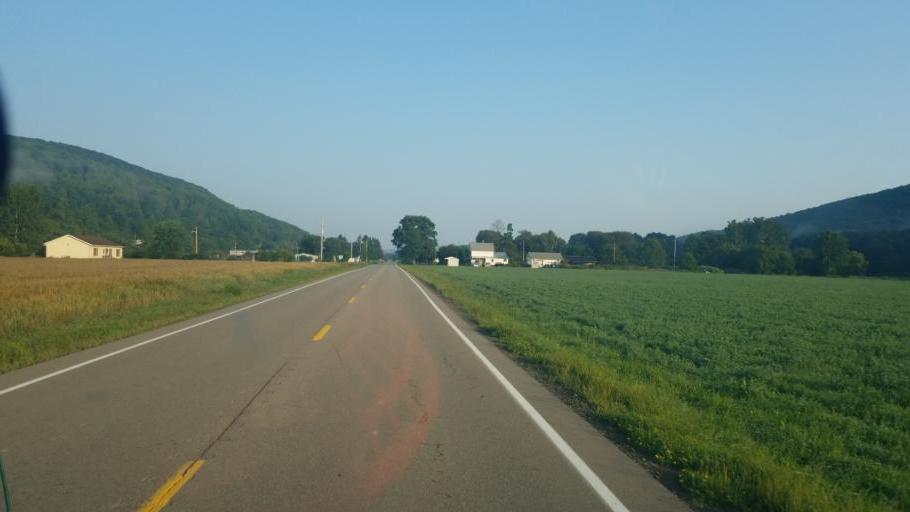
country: US
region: Pennsylvania
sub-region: Tioga County
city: Westfield
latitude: 41.9696
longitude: -77.4545
